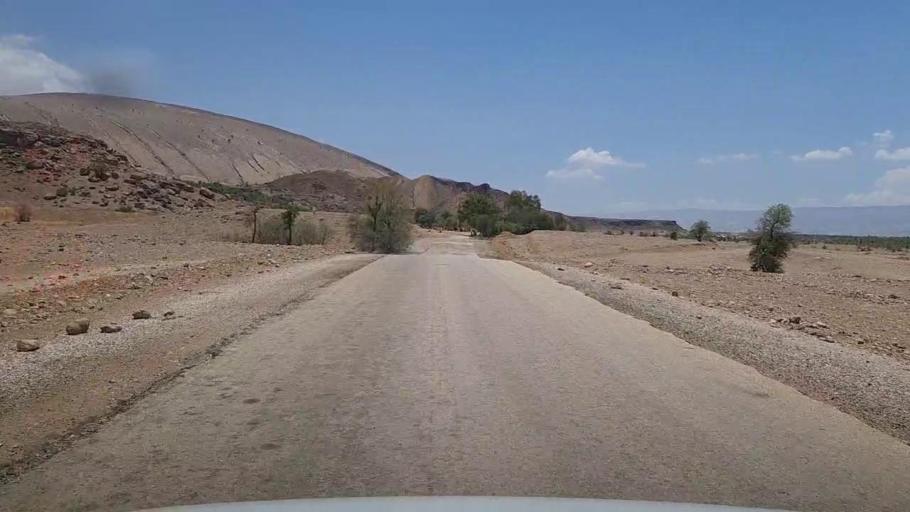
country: PK
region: Sindh
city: Bhan
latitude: 26.3045
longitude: 67.5358
